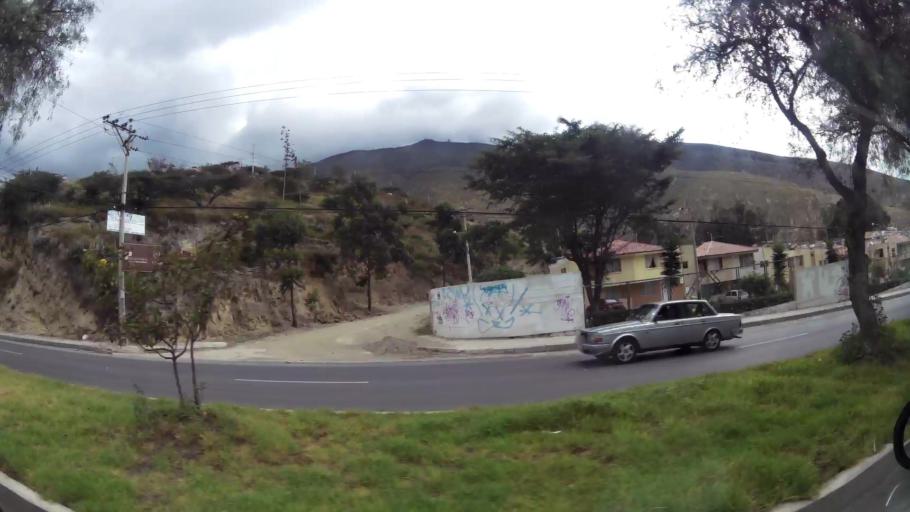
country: EC
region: Pichincha
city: Quito
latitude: -0.0272
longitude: -78.4516
